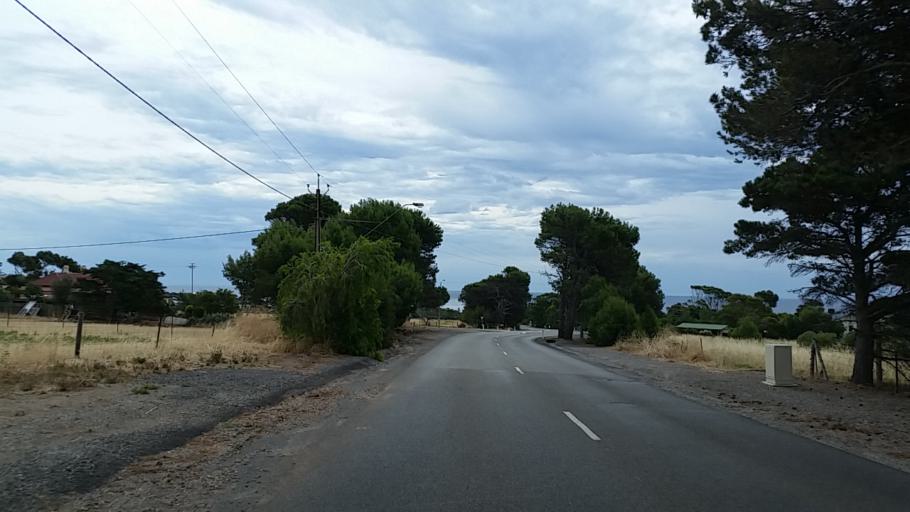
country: AU
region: South Australia
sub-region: Onkaparinga
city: Aldinga
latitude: -35.3290
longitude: 138.4637
